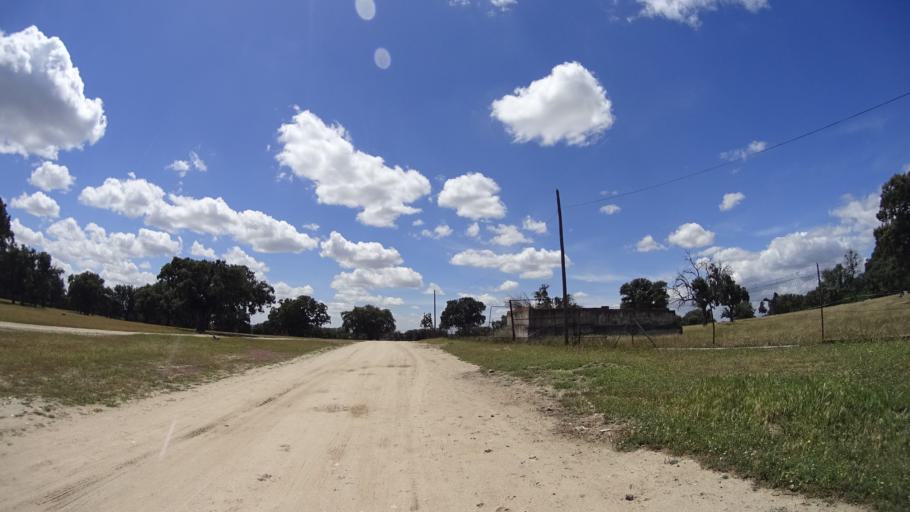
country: ES
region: Madrid
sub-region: Provincia de Madrid
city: Brunete
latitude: 40.4298
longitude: -3.9665
